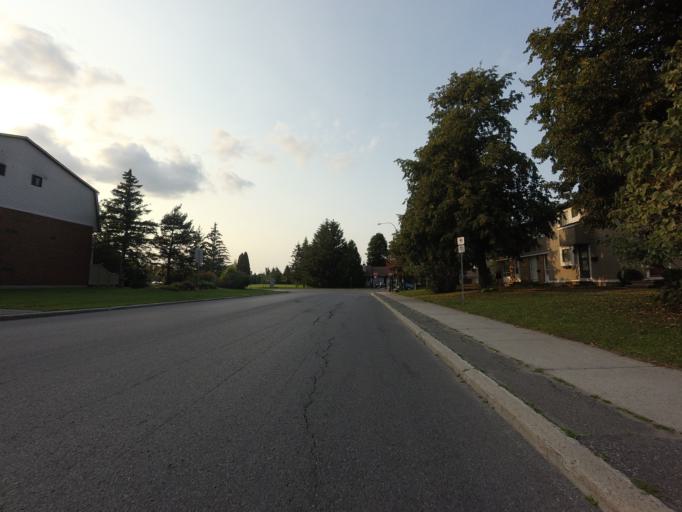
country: CA
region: Ontario
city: Bells Corners
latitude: 45.2801
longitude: -75.7579
